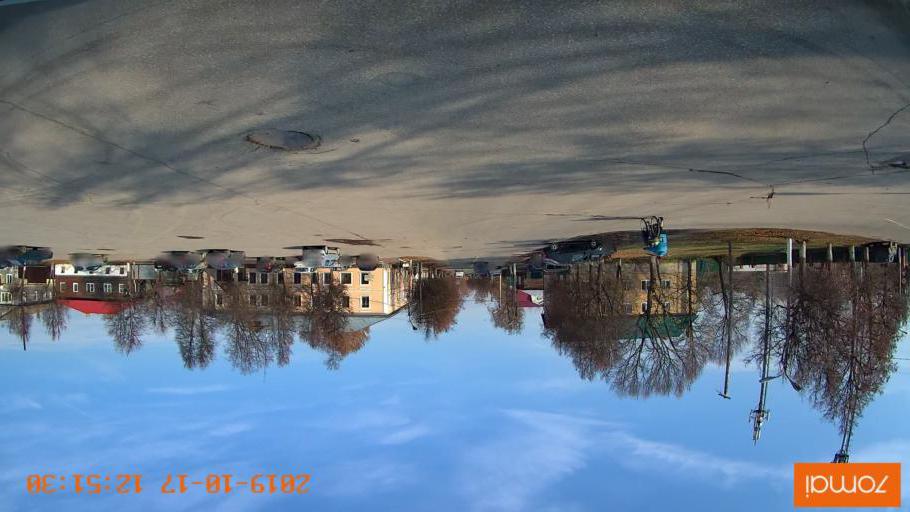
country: RU
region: Rjazan
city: Kasimov
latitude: 54.9407
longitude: 41.3921
